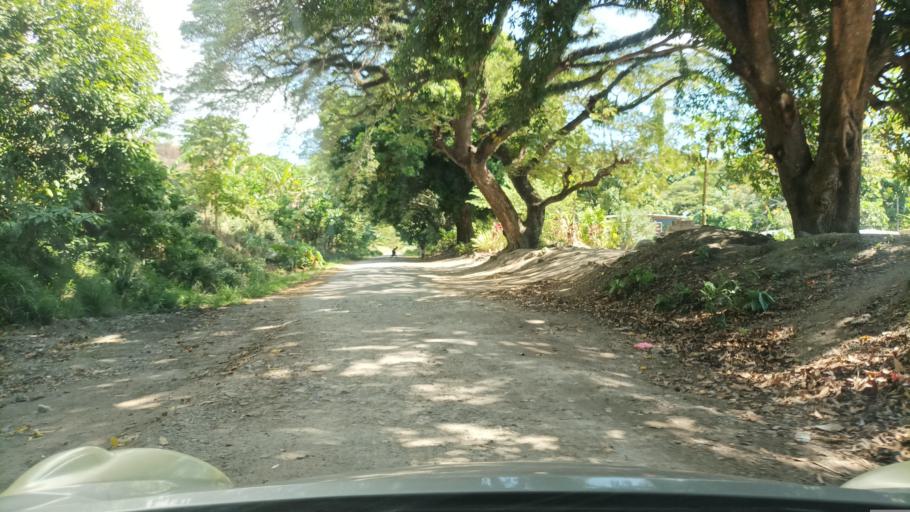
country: SB
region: Guadalcanal
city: Honiara
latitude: -9.2520
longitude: 159.7009
